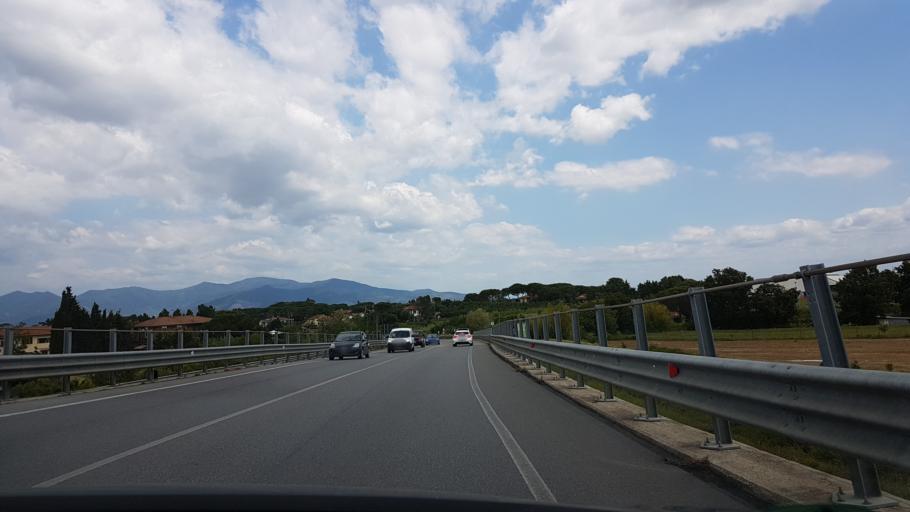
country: IT
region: Tuscany
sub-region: Provincia di Livorno
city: Collesalvetti
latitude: 43.5996
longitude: 10.4738
